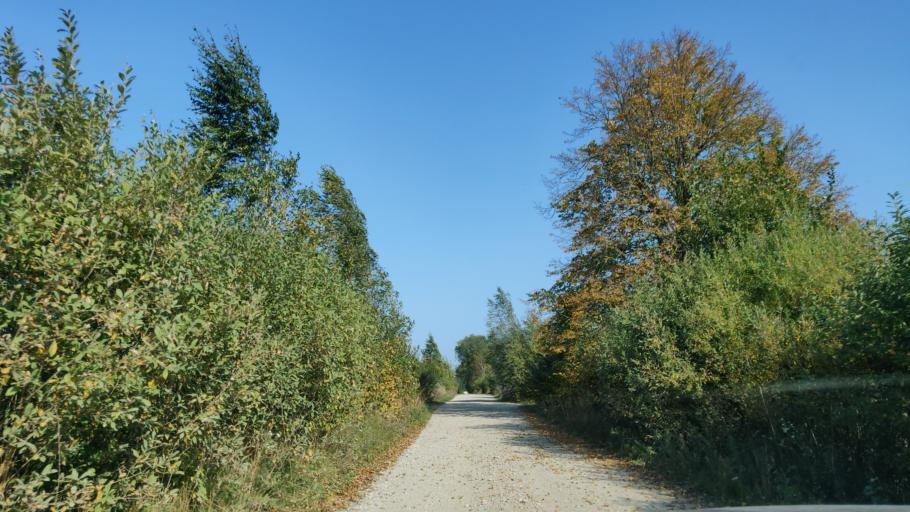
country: LT
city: Sirvintos
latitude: 54.9673
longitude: 24.8013
